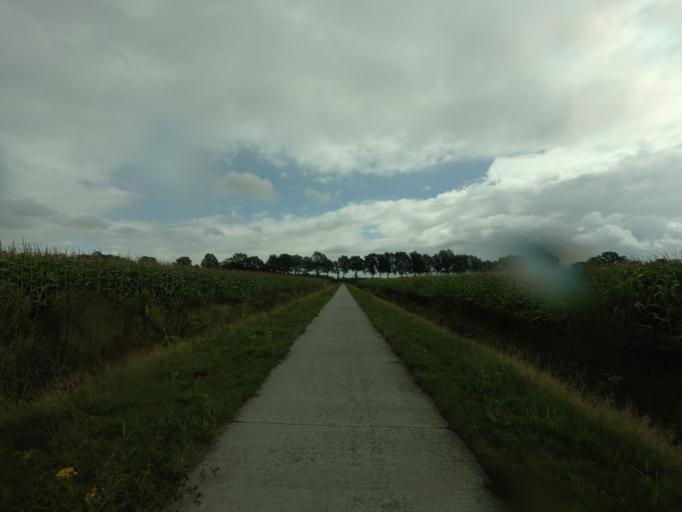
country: NL
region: Drenthe
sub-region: Gemeente Westerveld
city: Dwingeloo
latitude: 52.9750
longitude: 6.3600
